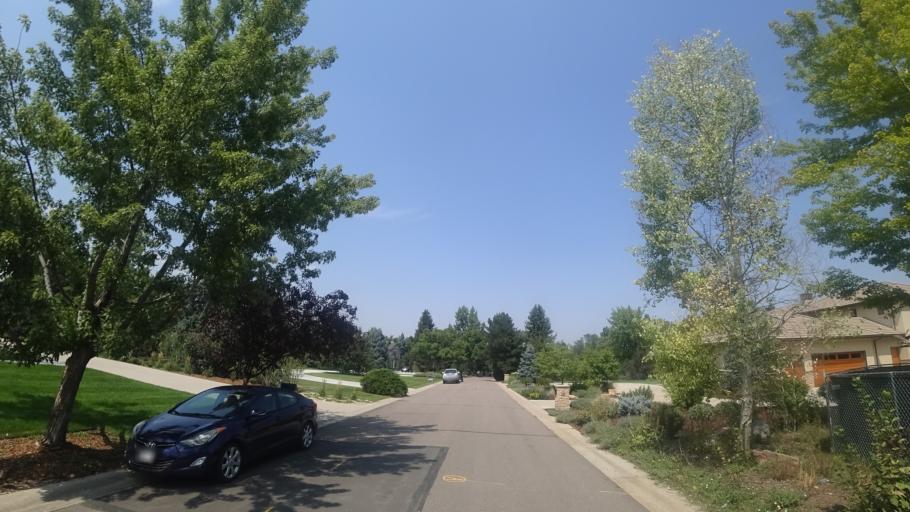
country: US
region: Colorado
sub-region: Arapahoe County
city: Greenwood Village
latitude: 39.6216
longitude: -104.9725
